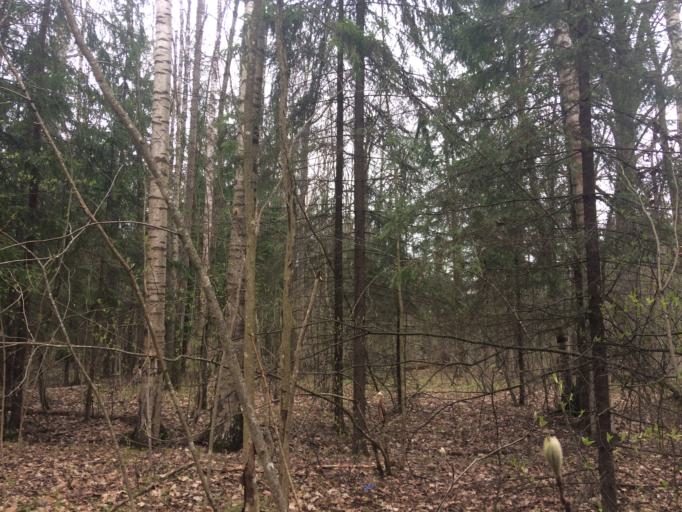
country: RU
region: St.-Petersburg
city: Petrodvorets
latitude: 59.8893
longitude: 29.8327
